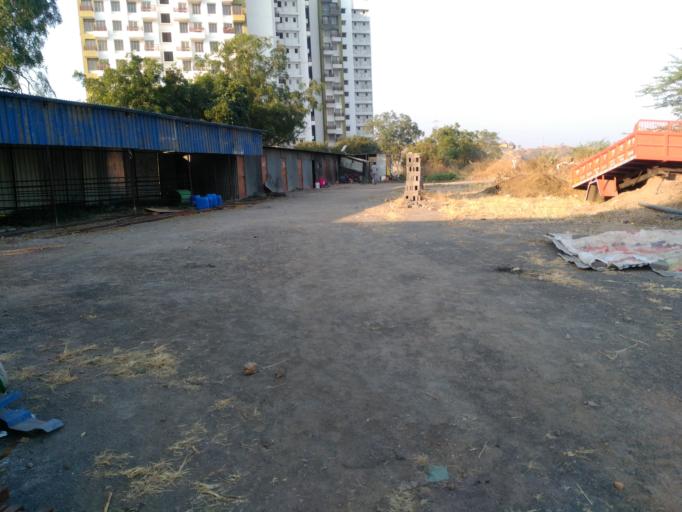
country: IN
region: Maharashtra
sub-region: Pune Division
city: Pune
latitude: 18.4285
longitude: 73.9024
